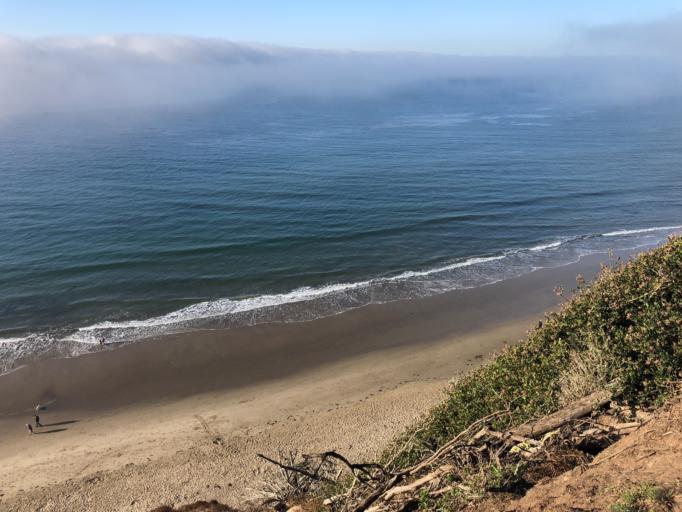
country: US
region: California
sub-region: Santa Barbara County
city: Santa Barbara
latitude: 34.4029
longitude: -119.7421
